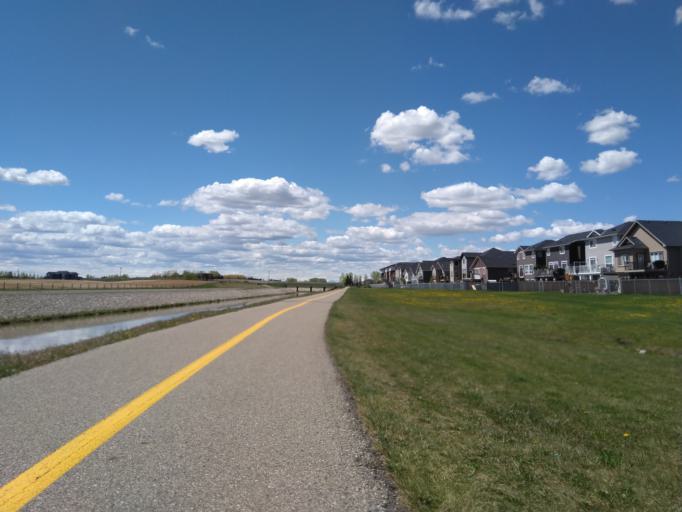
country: CA
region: Alberta
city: Chestermere
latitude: 51.0192
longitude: -113.8354
